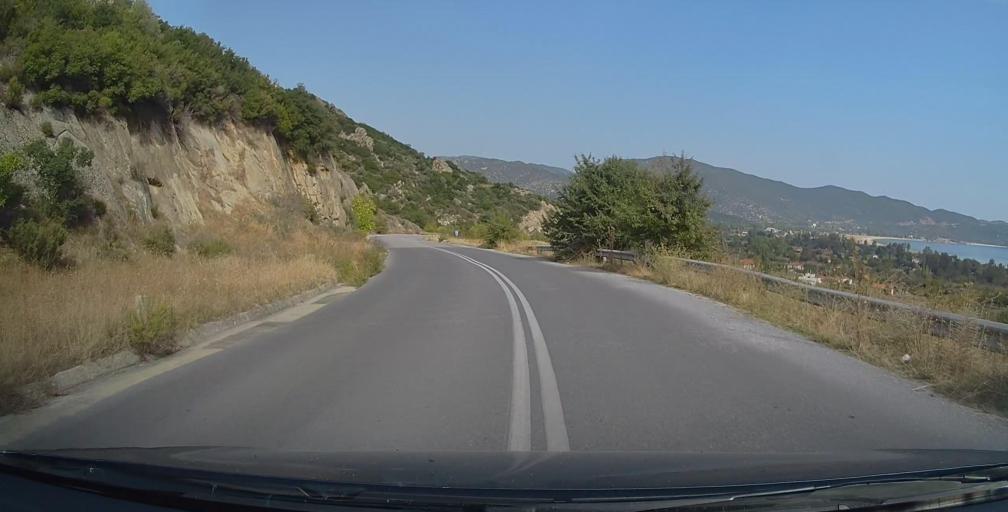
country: GR
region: Central Macedonia
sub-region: Nomos Chalkidikis
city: Sykia
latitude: 40.0273
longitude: 23.9883
